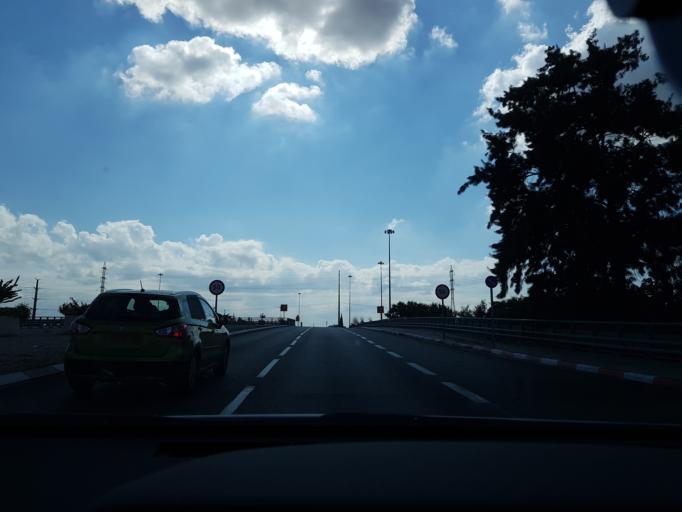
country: IL
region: Central District
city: Bet Dagan
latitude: 32.0026
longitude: 34.8021
